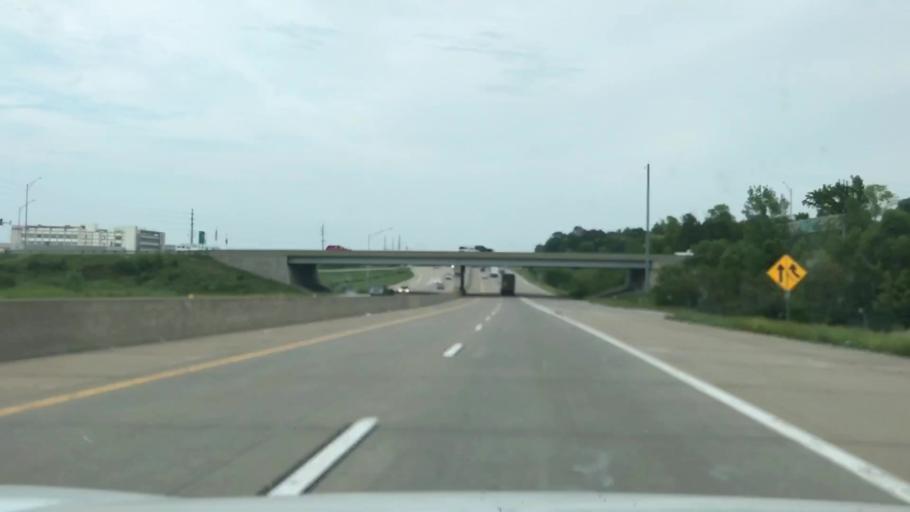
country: US
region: Missouri
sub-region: Saint Charles County
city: Weldon Spring
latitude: 38.7144
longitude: -90.7055
